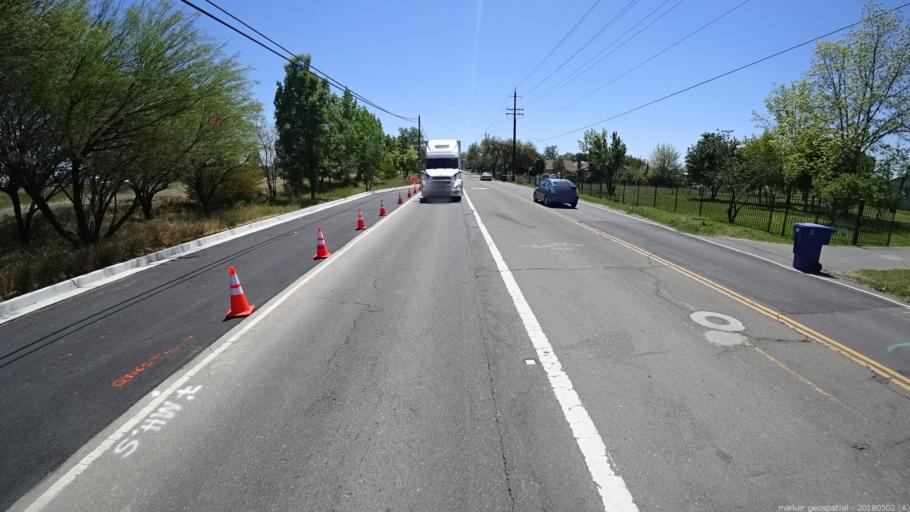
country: US
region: California
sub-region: Sacramento County
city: Rio Linda
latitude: 38.6512
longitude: -121.4478
